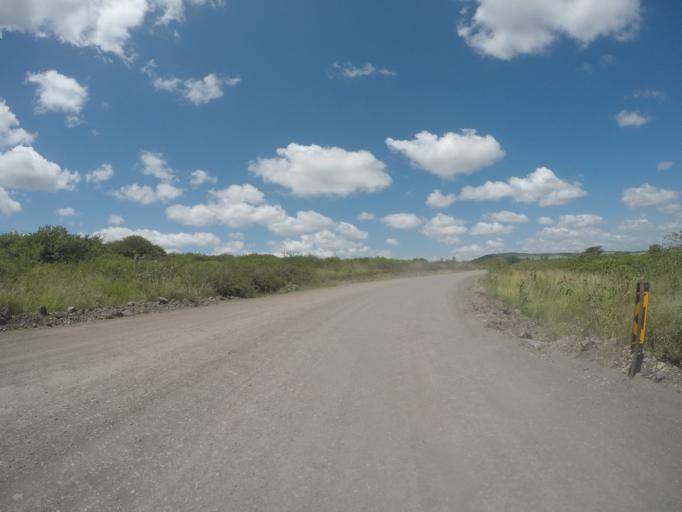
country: ZA
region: KwaZulu-Natal
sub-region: uThungulu District Municipality
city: Empangeni
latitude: -28.6604
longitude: 31.7814
